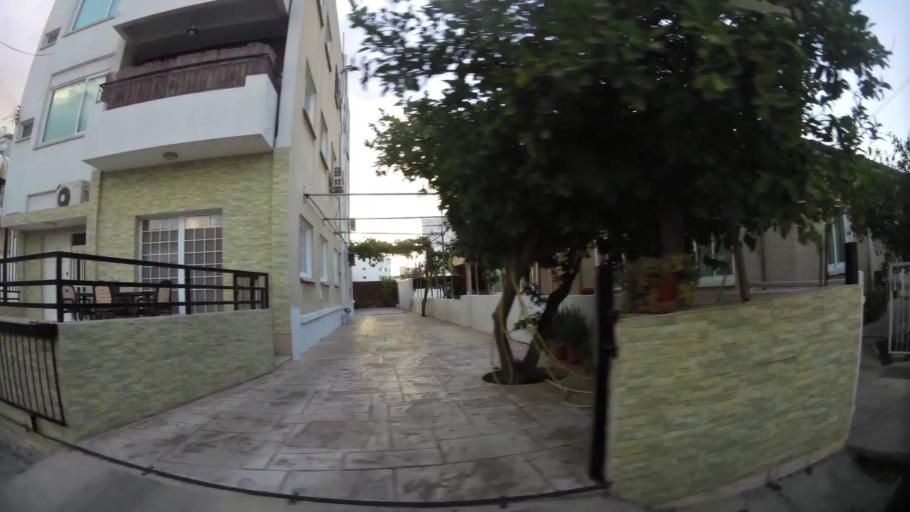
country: CY
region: Lefkosia
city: Nicosia
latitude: 35.1322
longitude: 33.3320
